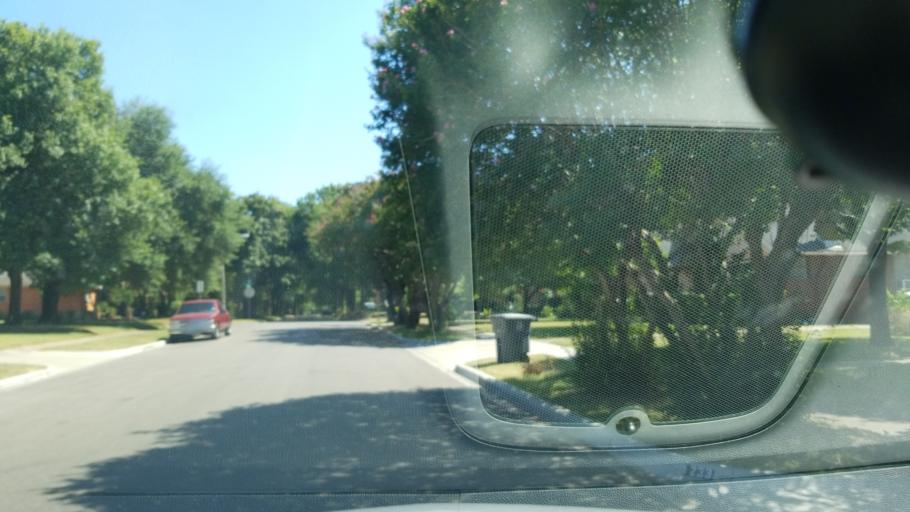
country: US
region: Texas
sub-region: Dallas County
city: Cockrell Hill
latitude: 32.7321
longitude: -96.8544
